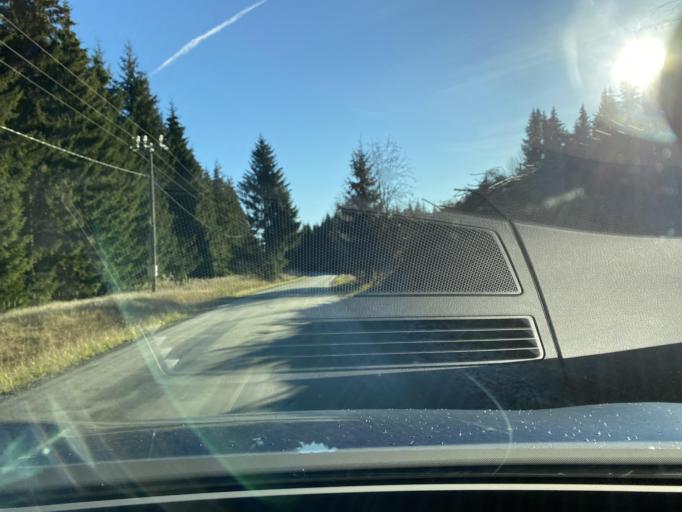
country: FI
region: Pirkanmaa
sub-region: Etelae-Pirkanmaa
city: Toijala
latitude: 61.0298
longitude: 23.8045
